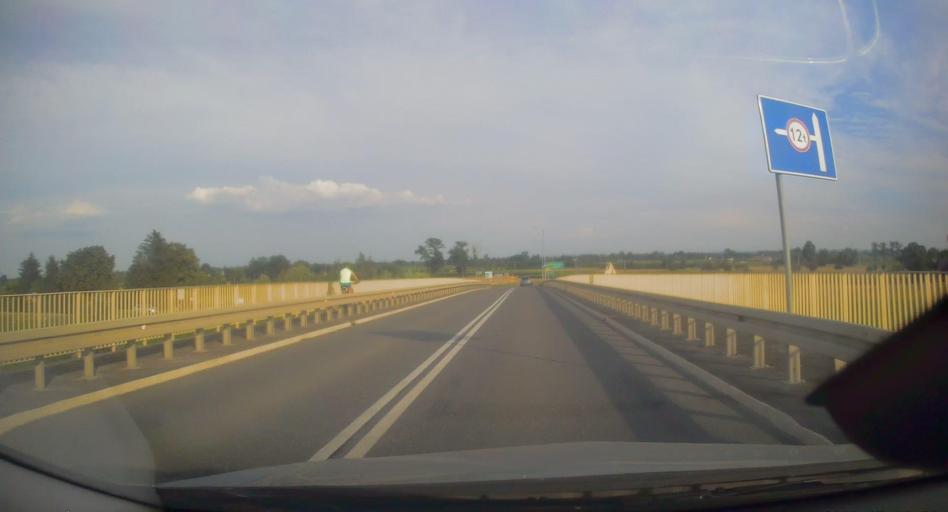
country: PL
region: Lesser Poland Voivodeship
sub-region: Powiat brzeski
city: Szczurowa
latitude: 50.1527
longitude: 20.6102
